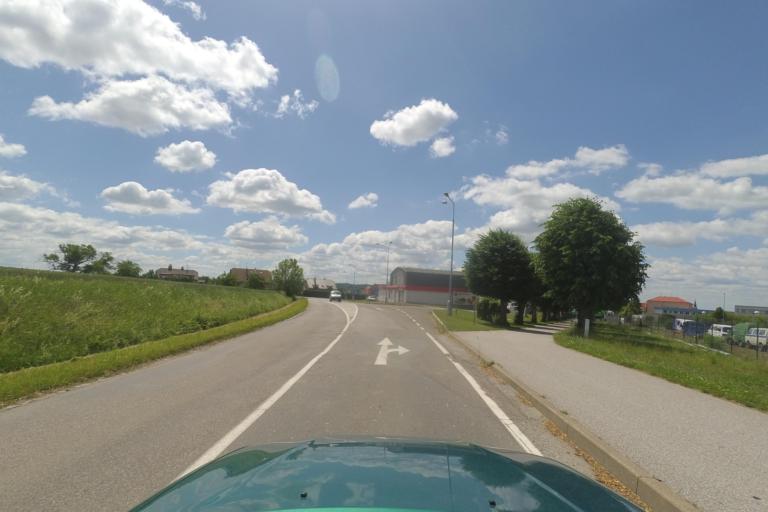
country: CZ
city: Dobruska
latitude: 50.2967
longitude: 16.1687
